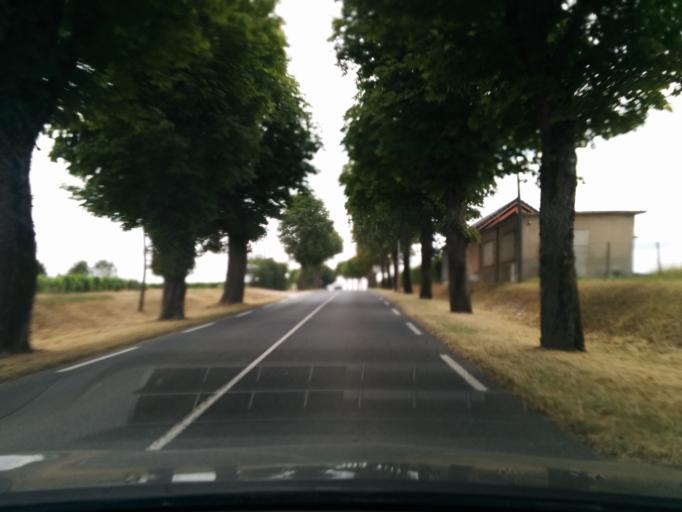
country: FR
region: Centre
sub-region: Departement du Cher
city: Sancerre
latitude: 47.3238
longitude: 2.8226
